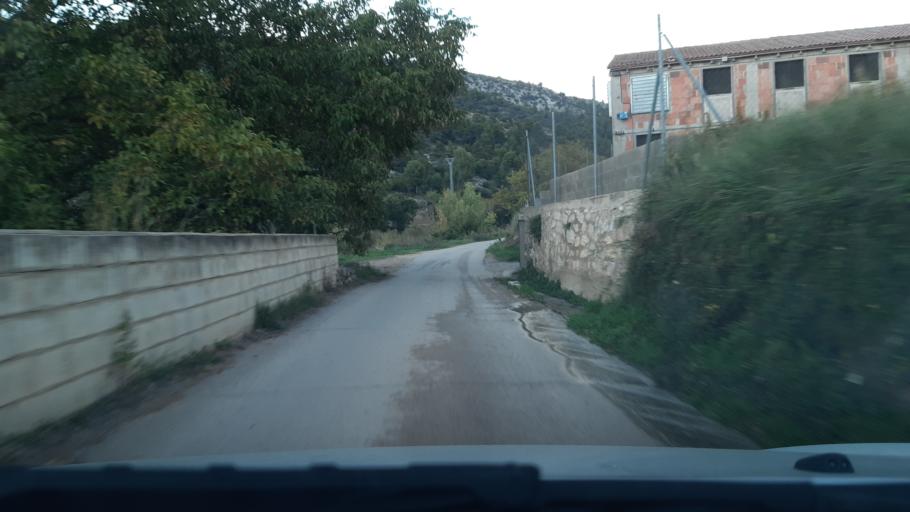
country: ES
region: Aragon
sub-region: Provincia de Teruel
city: Valderrobres
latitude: 40.8385
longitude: 0.1921
